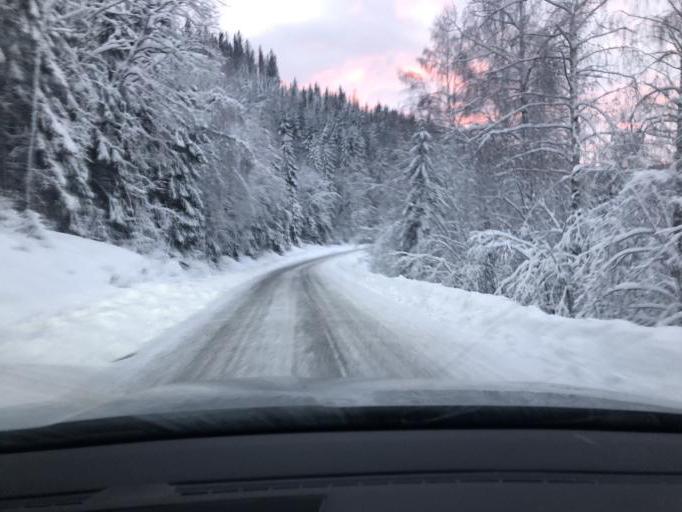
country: SE
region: Vaesternorrland
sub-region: Kramfors Kommun
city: Nordingra
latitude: 62.9196
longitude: 18.2213
